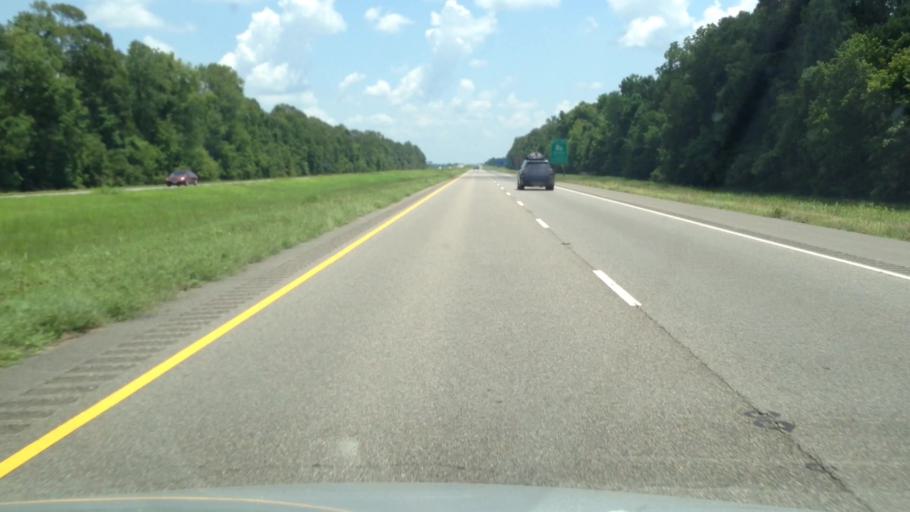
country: US
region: Louisiana
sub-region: Avoyelles Parish
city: Bunkie
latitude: 30.9642
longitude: -92.2865
